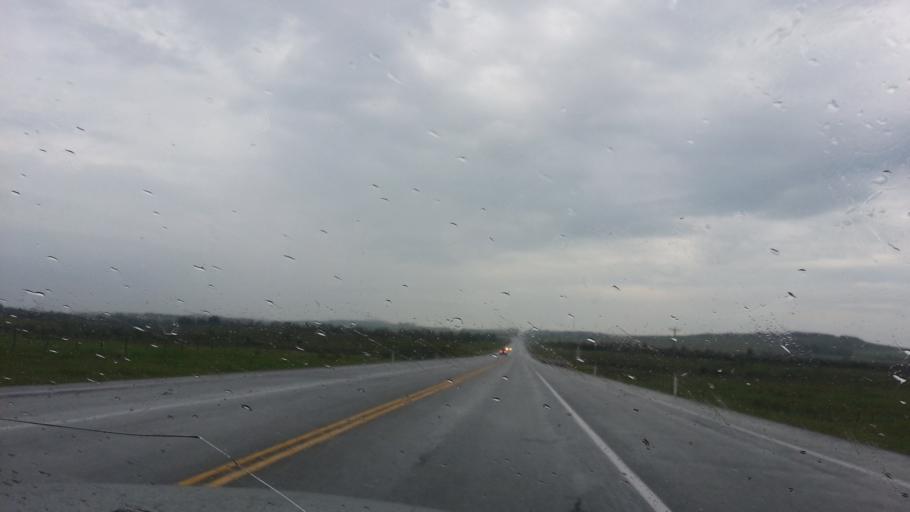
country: CA
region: Alberta
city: Cochrane
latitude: 51.0676
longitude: -114.4668
